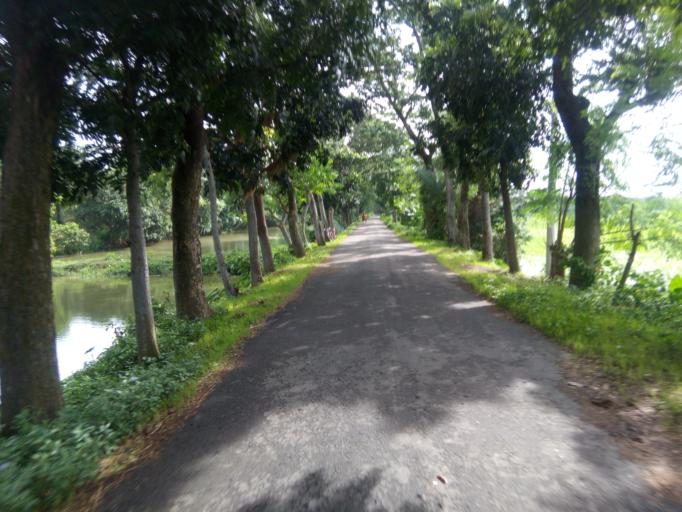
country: BD
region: Khulna
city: Kalia
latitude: 22.9558
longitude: 89.5518
